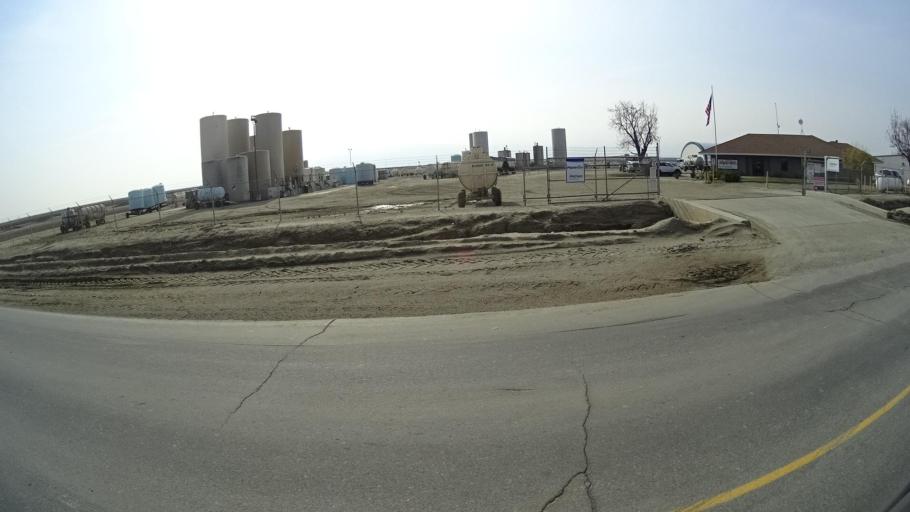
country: US
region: California
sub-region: Kern County
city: Greenfield
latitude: 35.0952
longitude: -119.0218
